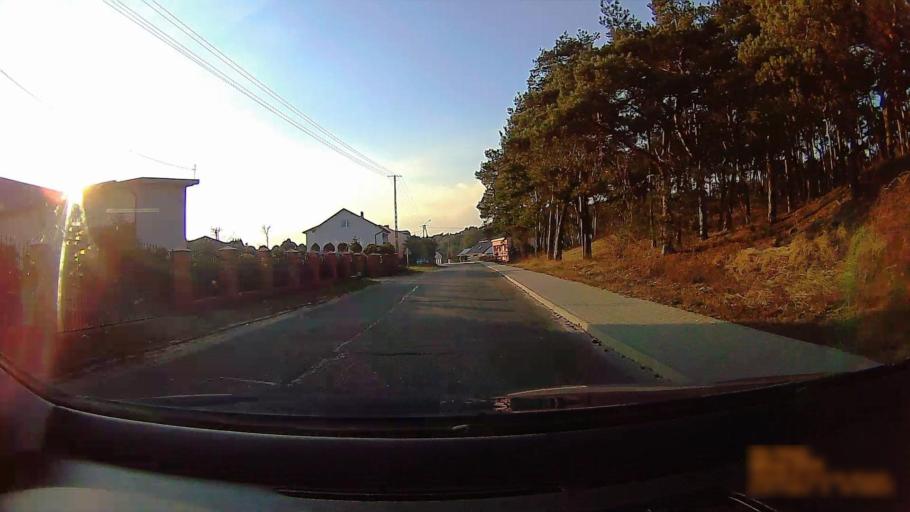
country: PL
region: Greater Poland Voivodeship
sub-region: Konin
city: Konin
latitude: 52.1969
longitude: 18.3134
